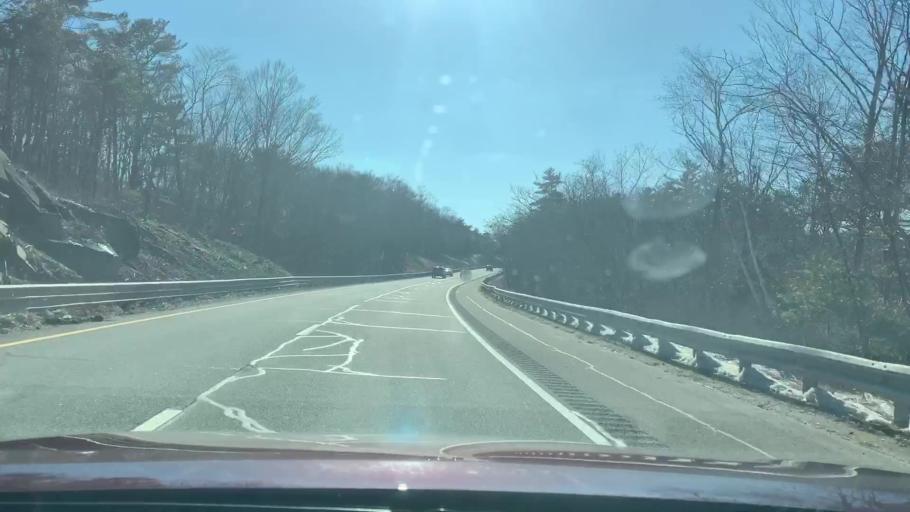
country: US
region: Massachusetts
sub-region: Essex County
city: Essex
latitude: 42.6082
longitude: -70.7377
